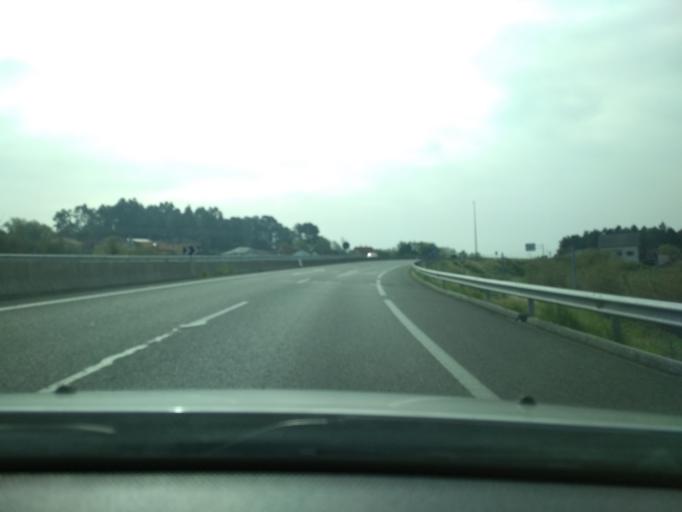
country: ES
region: Galicia
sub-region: Provincia da Coruna
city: Rianxo
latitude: 42.6734
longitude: -8.8313
